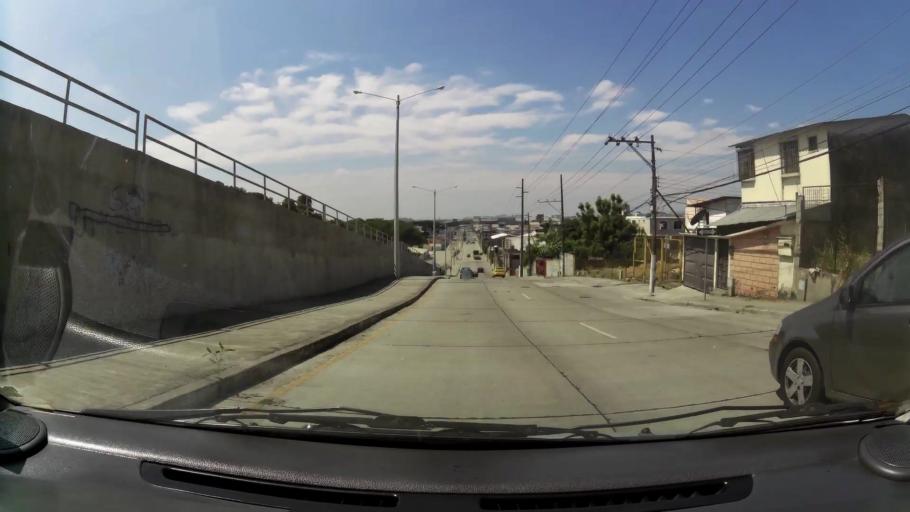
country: EC
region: Guayas
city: Guayaquil
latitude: -2.1357
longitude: -79.9182
